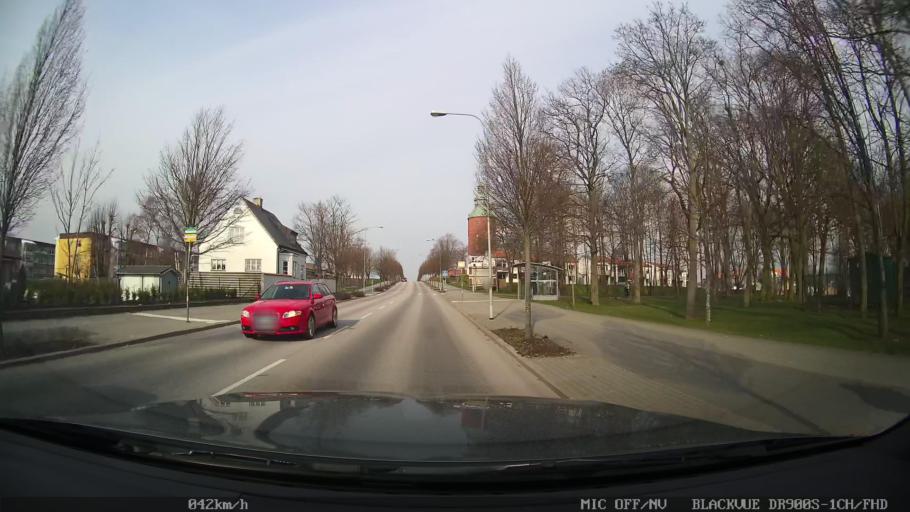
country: SE
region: Skane
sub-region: Ystads Kommun
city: Ystad
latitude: 55.4373
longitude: 13.8251
